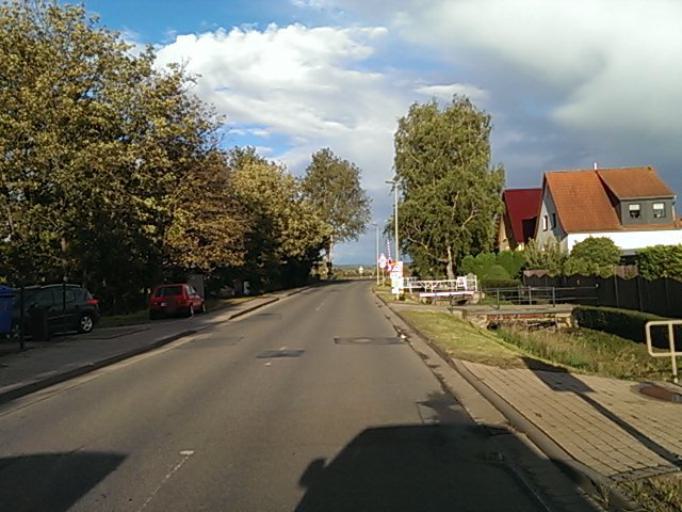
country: DE
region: Thuringia
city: Griefstedt
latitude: 51.2020
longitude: 11.1552
